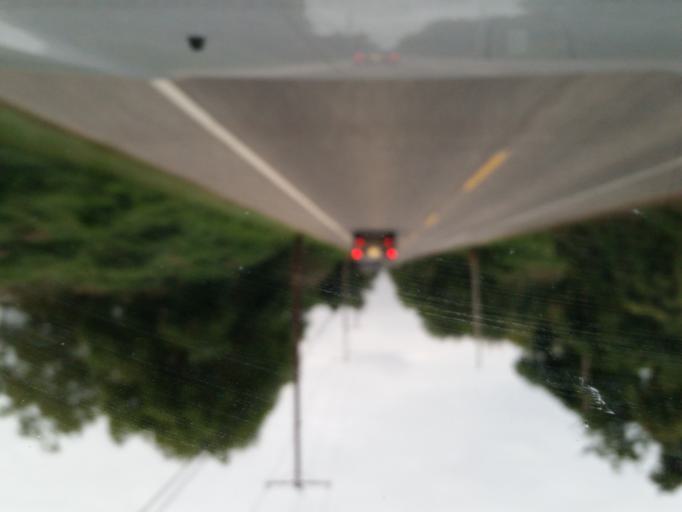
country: US
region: New Jersey
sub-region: Cape May County
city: West Cape May
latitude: 38.9413
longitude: -74.9568
